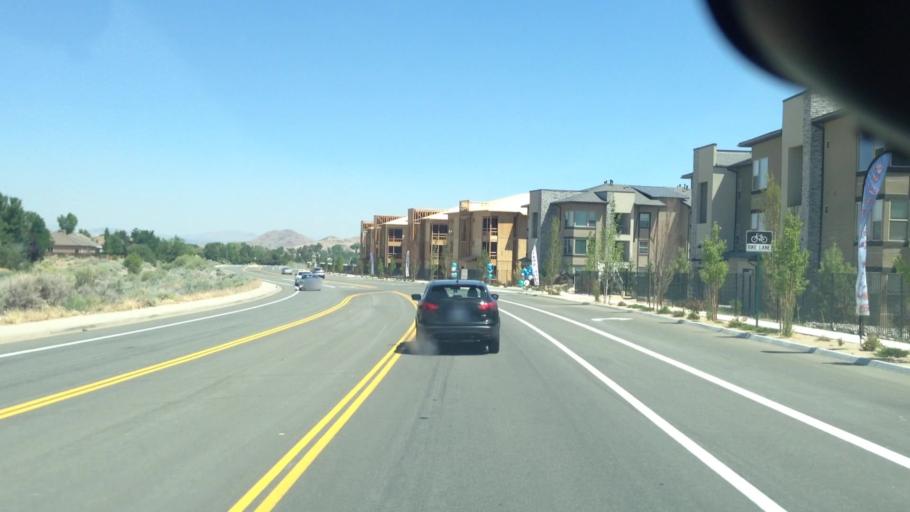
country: US
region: Nevada
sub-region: Washoe County
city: Sparks
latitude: 39.4120
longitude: -119.7596
